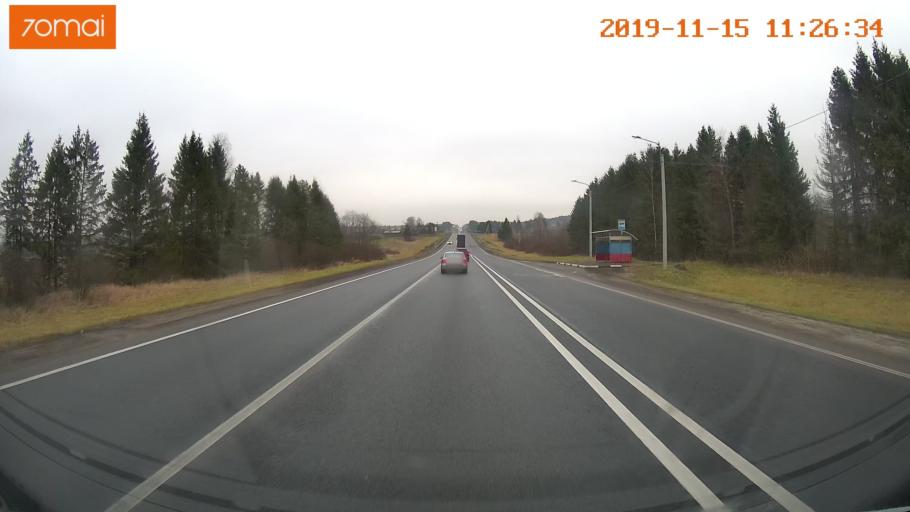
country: RU
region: Vologda
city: Molochnoye
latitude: 59.1674
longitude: 39.4487
